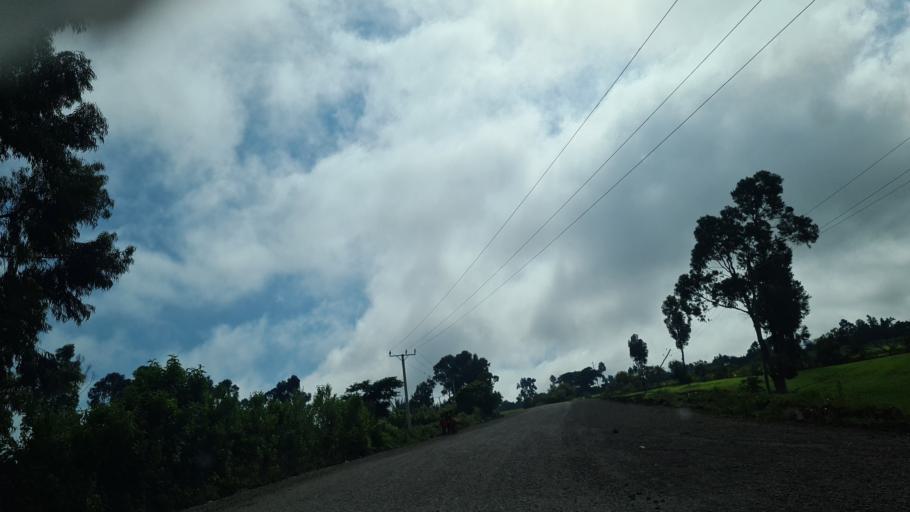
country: ET
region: Oromiya
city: Huruta
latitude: 8.1276
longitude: 39.3774
